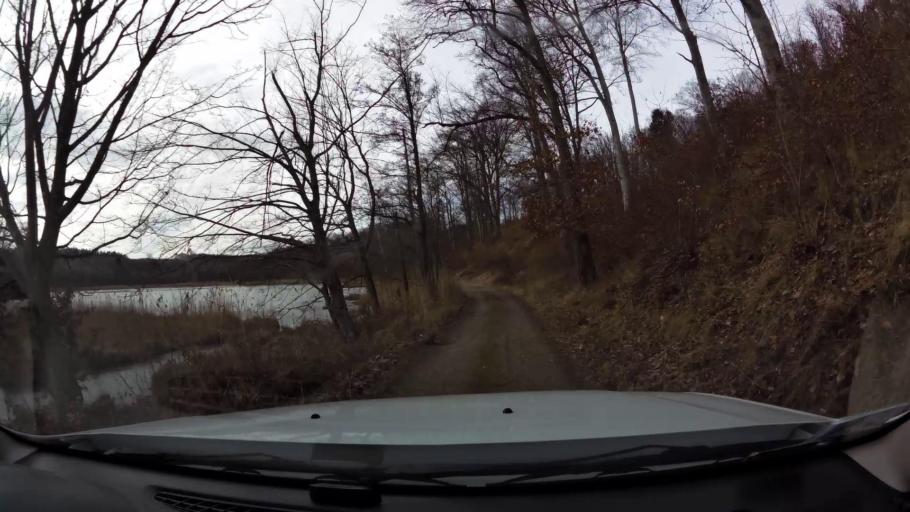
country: PL
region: West Pomeranian Voivodeship
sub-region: Powiat drawski
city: Drawsko Pomorskie
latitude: 53.4965
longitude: 15.7175
